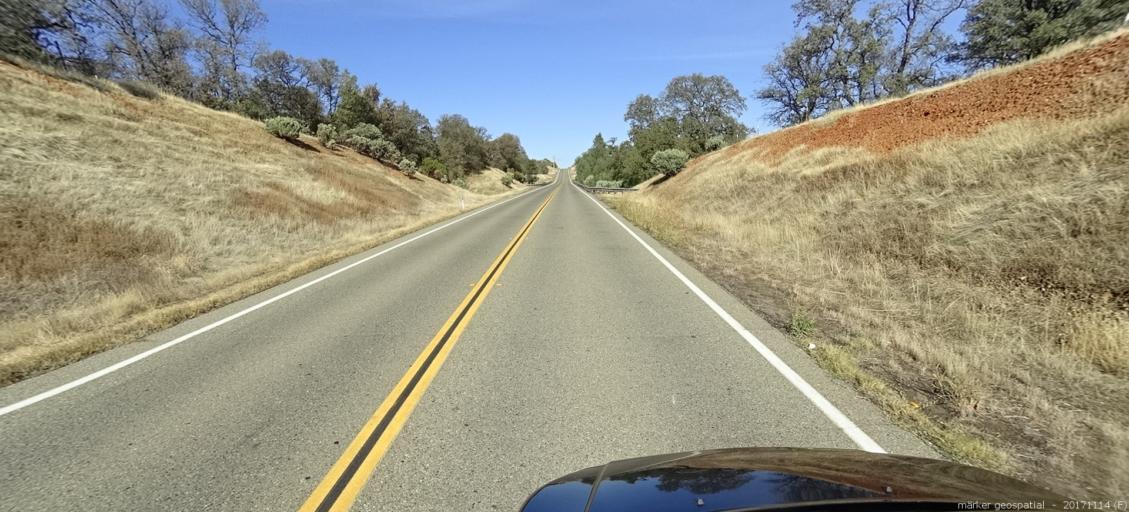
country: US
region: California
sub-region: Shasta County
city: Anderson
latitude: 40.4017
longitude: -122.4063
